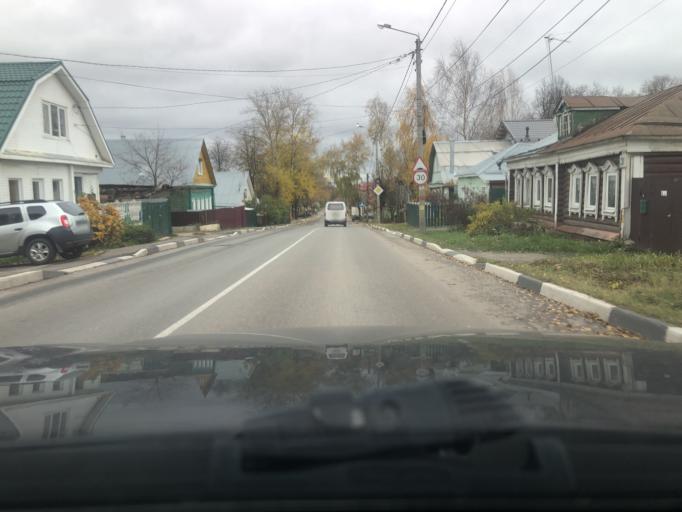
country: RU
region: Moskovskaya
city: Sergiyev Posad
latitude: 56.3167
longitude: 38.1238
